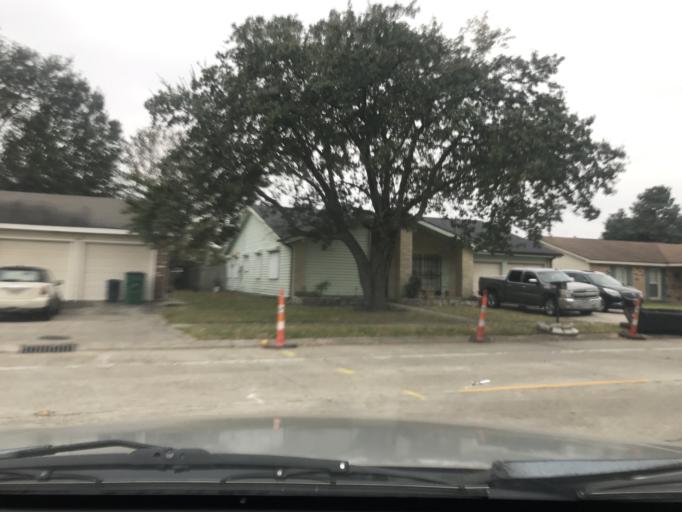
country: US
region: Louisiana
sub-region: Jefferson Parish
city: Woodmere
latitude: 29.8601
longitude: -90.0786
